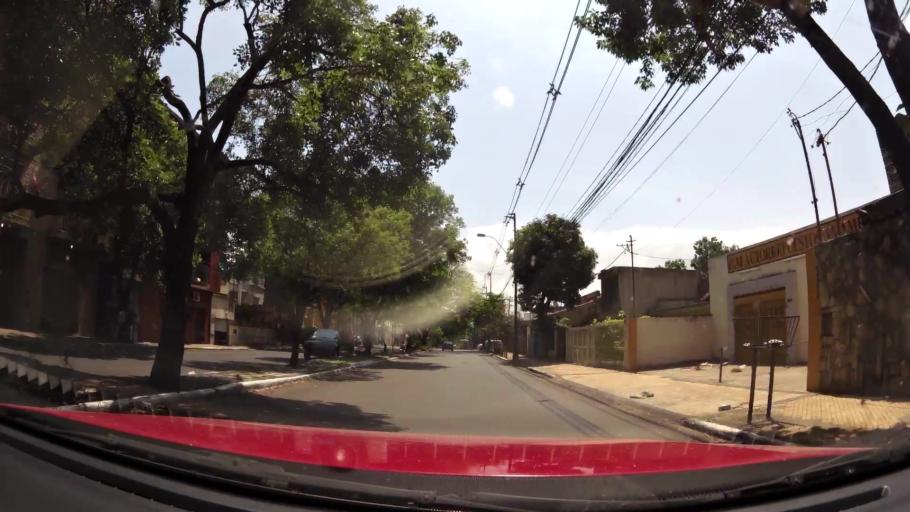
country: PY
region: Asuncion
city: Asuncion
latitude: -25.2942
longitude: -57.6333
